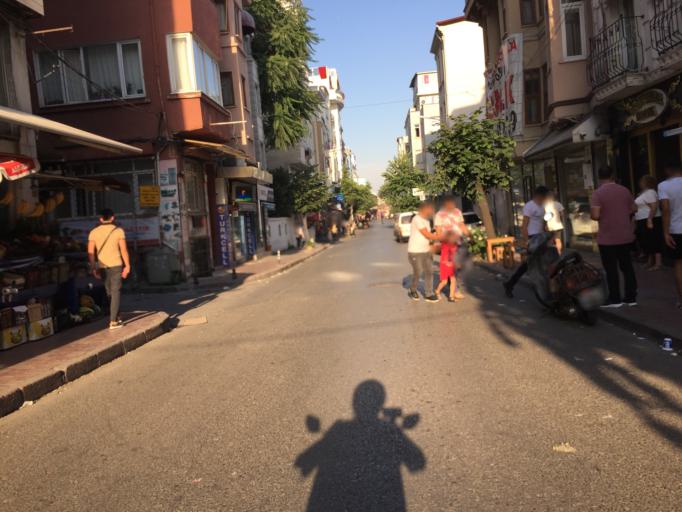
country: TR
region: Istanbul
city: Eminoenue
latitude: 41.0052
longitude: 28.9638
